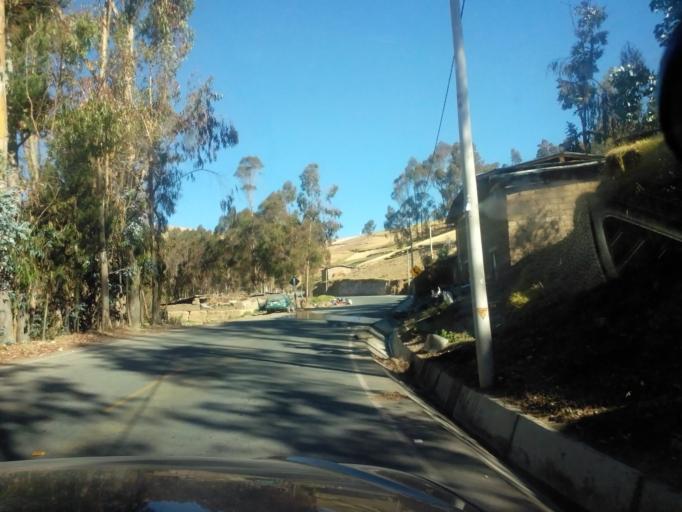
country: PE
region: Apurimac
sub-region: Provincia de Andahuaylas
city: Pacucha
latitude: -13.6530
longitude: -73.2943
